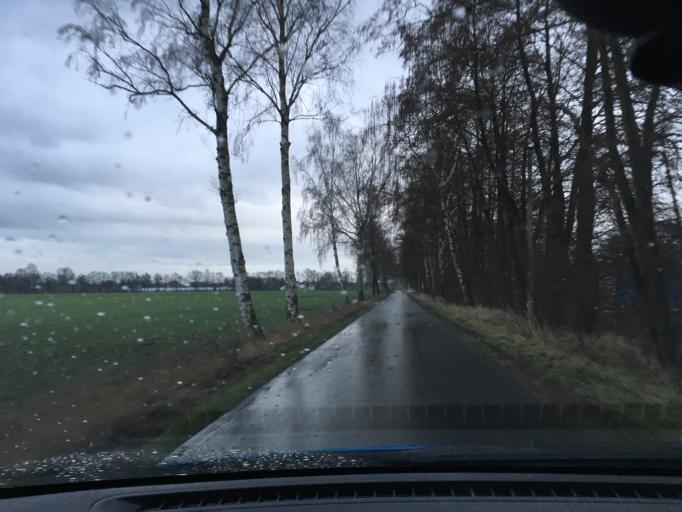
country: DE
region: Lower Saxony
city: Ludersburg
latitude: 53.3159
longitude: 10.6028
